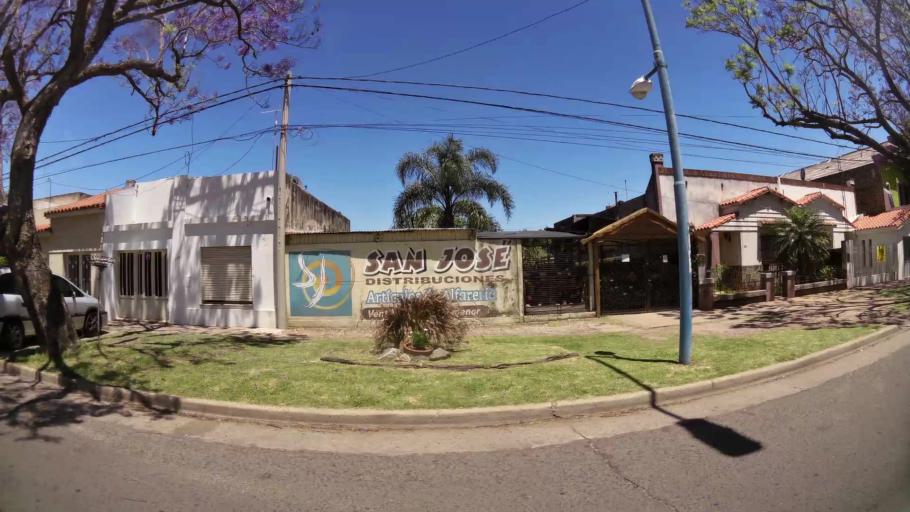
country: AR
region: Santa Fe
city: Rafaela
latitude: -31.2566
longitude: -61.4693
